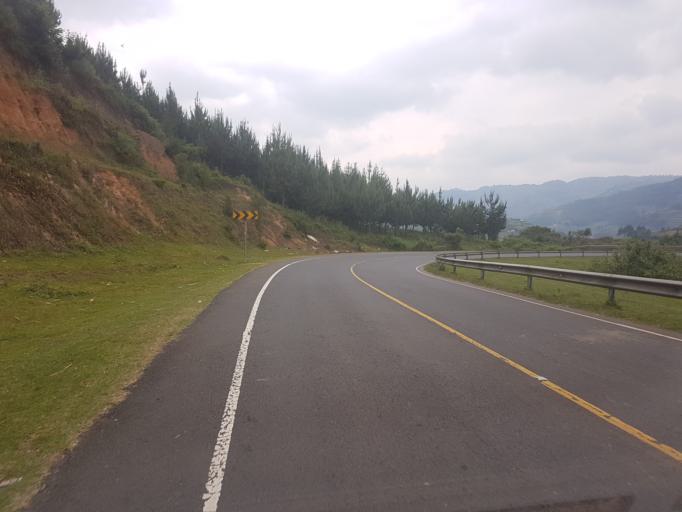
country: UG
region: Western Region
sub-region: Kabale District
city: Kabale
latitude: -1.2119
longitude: 29.8317
